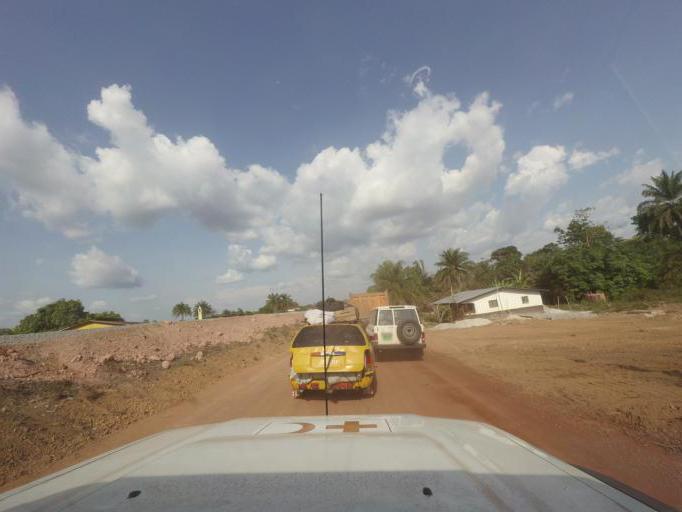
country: LR
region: Bong
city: Gbarnga
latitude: 7.0419
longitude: -9.5360
